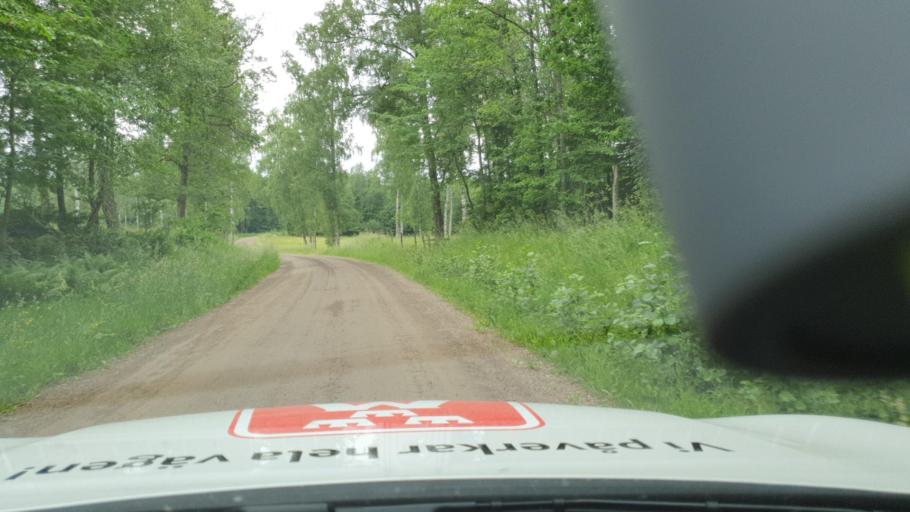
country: SE
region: Vaestra Goetaland
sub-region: Hjo Kommun
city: Hjo
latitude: 58.2016
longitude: 14.1775
